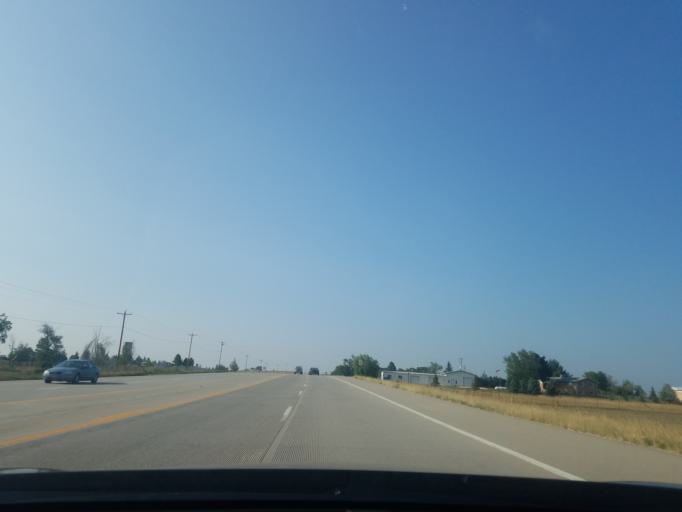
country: US
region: Colorado
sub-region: Boulder County
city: Longmont
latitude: 40.2365
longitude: -105.1023
